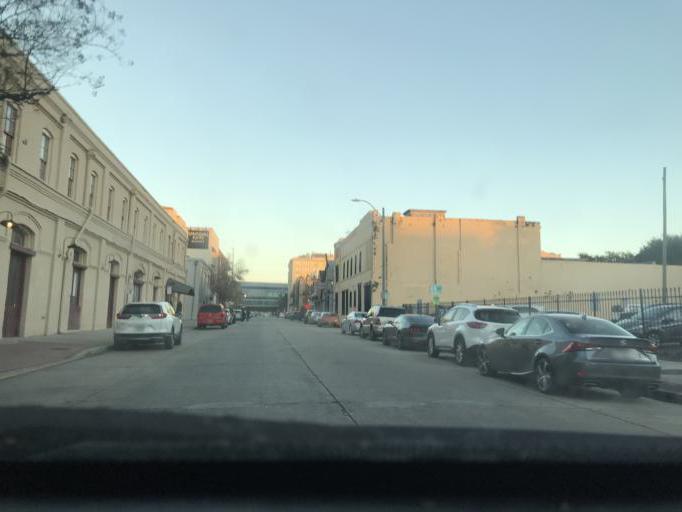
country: US
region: Louisiana
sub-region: Orleans Parish
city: New Orleans
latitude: 29.9433
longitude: -90.0674
